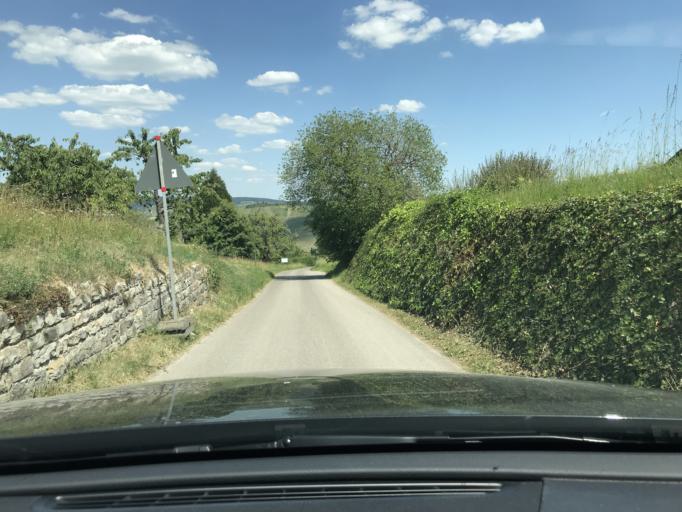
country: DE
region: Baden-Wuerttemberg
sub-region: Regierungsbezirk Stuttgart
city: Weinstadt-Endersbach
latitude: 48.7939
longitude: 9.3796
